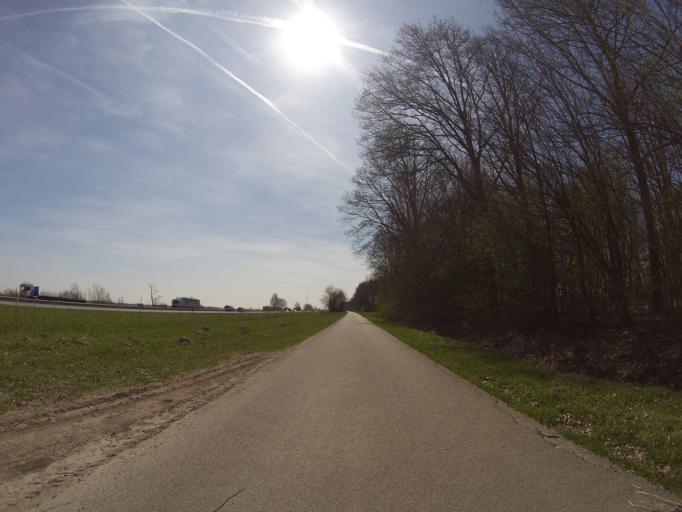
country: NL
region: Gelderland
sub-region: Gemeente Ermelo
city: Horst
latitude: 52.3020
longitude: 5.5549
